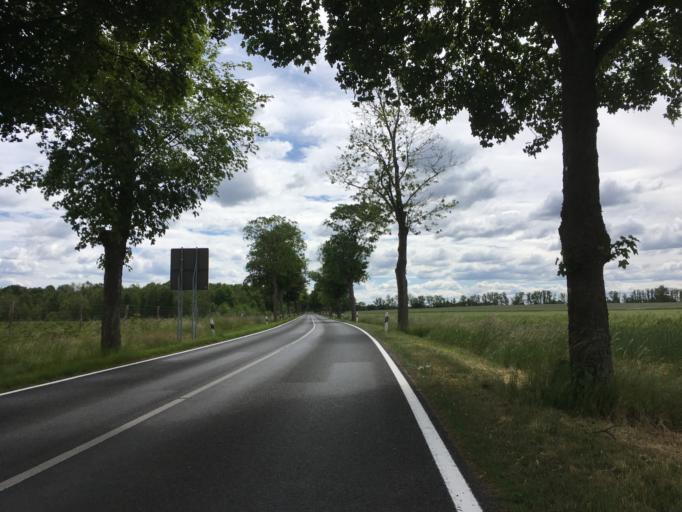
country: DE
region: Brandenburg
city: Melchow
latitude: 52.7490
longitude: 13.6875
